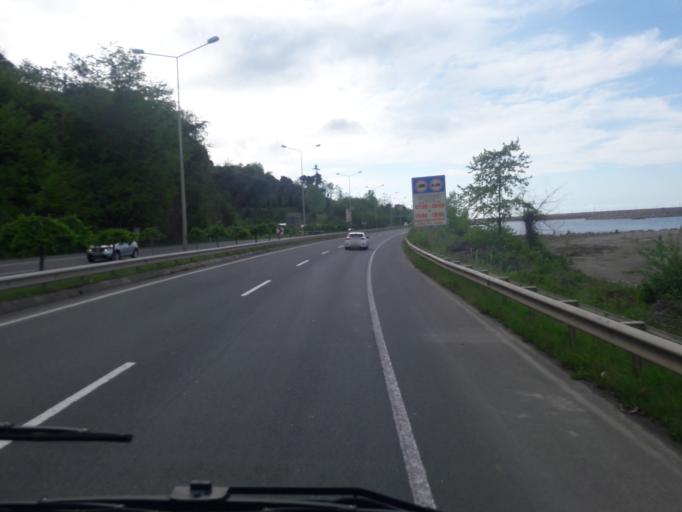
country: TR
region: Giresun
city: Piraziz
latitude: 40.9582
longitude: 38.1105
